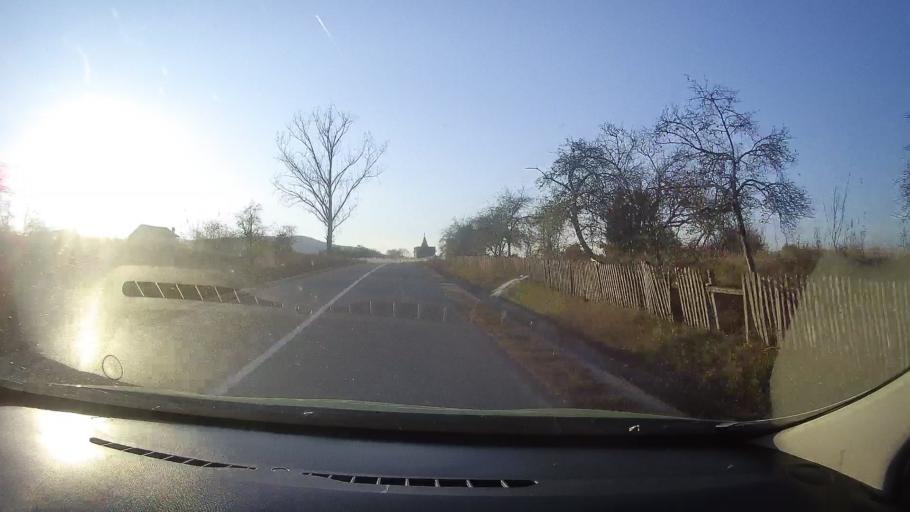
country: RO
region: Timis
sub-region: Comuna Fardea
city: Fardea
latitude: 45.7430
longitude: 22.1569
